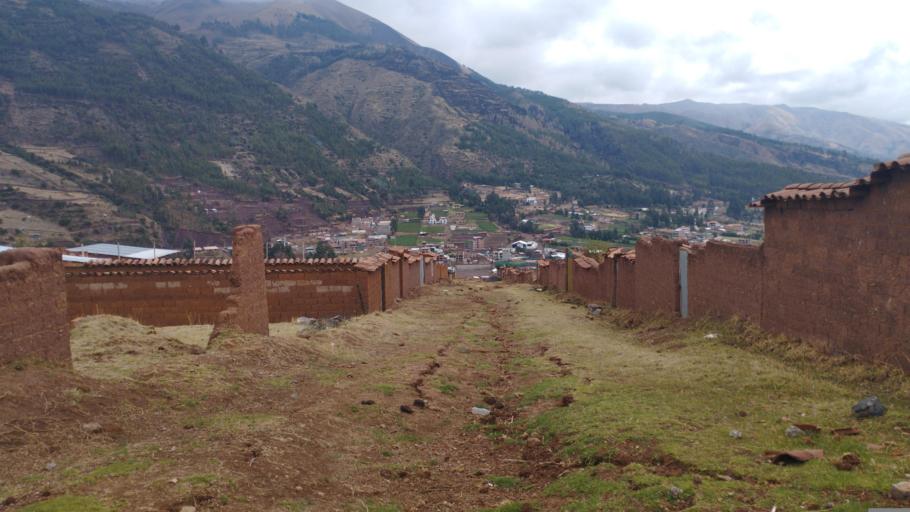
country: PE
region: Cusco
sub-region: Provincia de Cusco
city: Cusco
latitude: -13.5189
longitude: -71.9157
